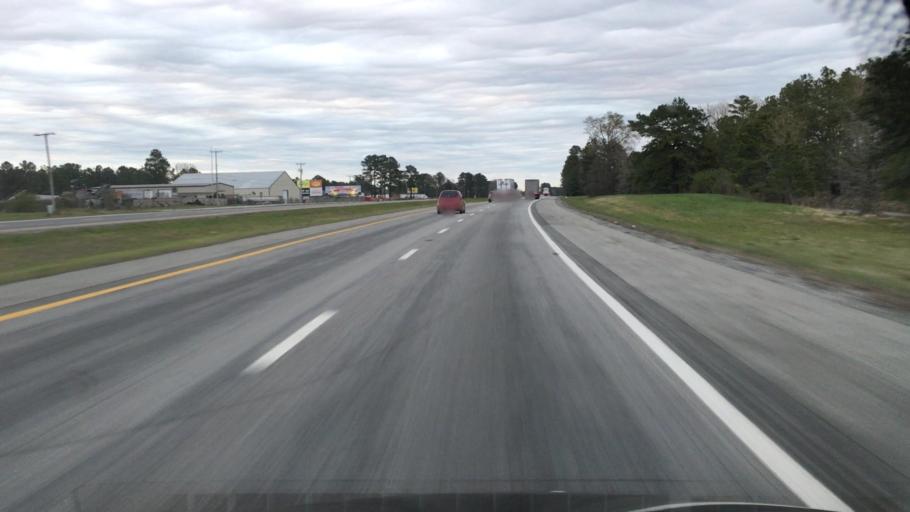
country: US
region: Virginia
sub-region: City of Emporia
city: Emporia
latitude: 36.8277
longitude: -77.4519
